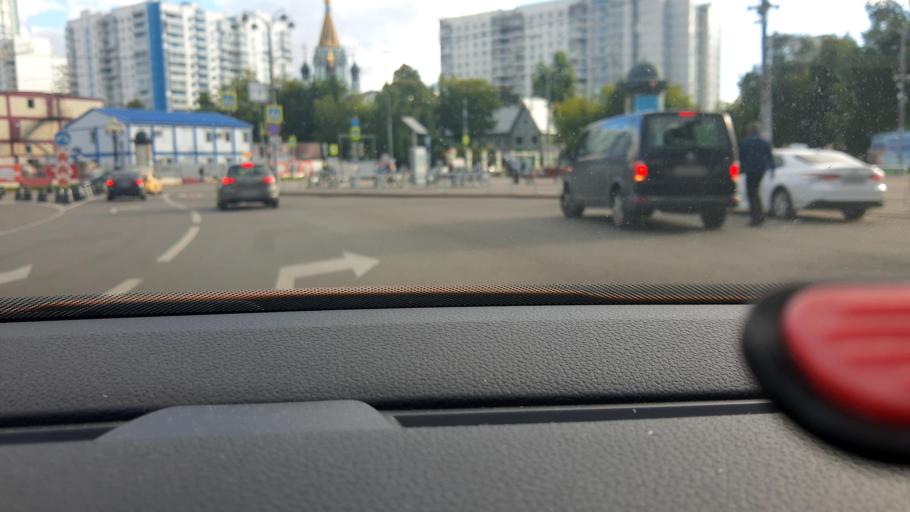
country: RU
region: Moscow
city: Sokol'niki
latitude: 55.7928
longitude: 37.6771
